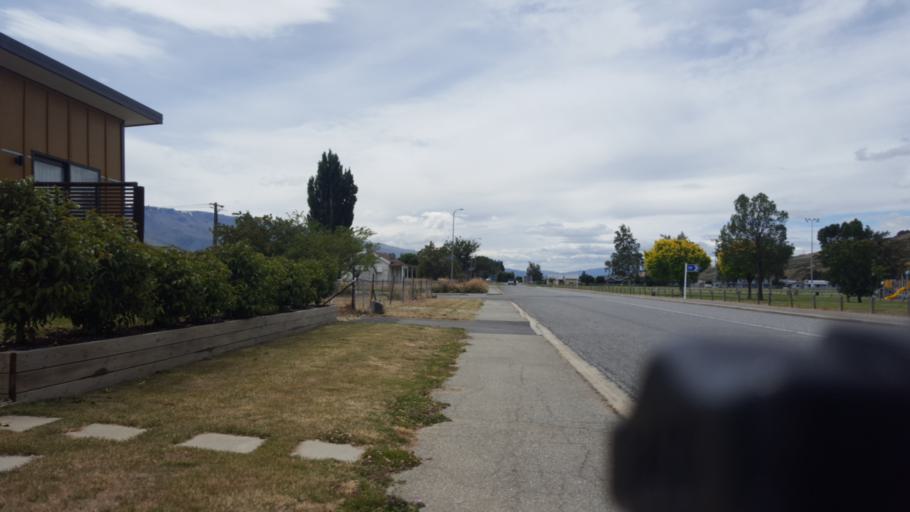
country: NZ
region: Otago
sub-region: Queenstown-Lakes District
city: Wanaka
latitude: -45.0436
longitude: 169.2134
